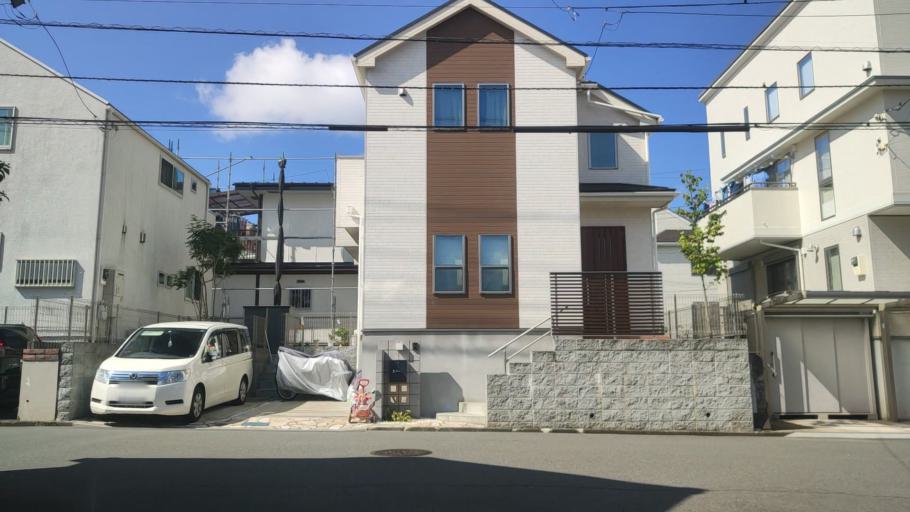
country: JP
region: Kanagawa
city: Yokohama
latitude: 35.4125
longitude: 139.5750
